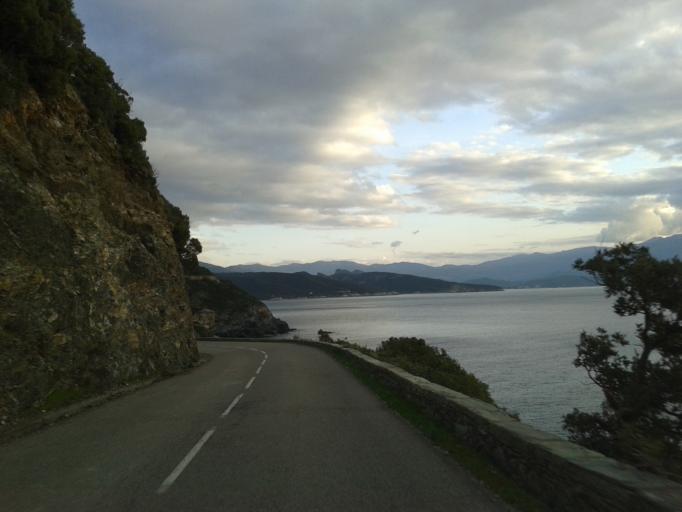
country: FR
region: Corsica
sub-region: Departement de la Haute-Corse
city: Saint-Florent
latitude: 42.7642
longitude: 9.3378
